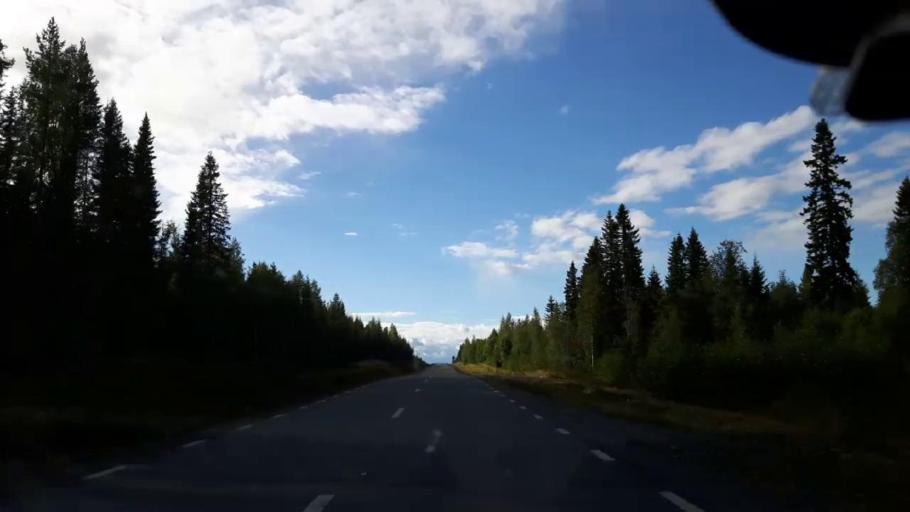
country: SE
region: Jaemtland
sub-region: Stroemsunds Kommun
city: Stroemsund
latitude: 63.5731
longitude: 15.7604
